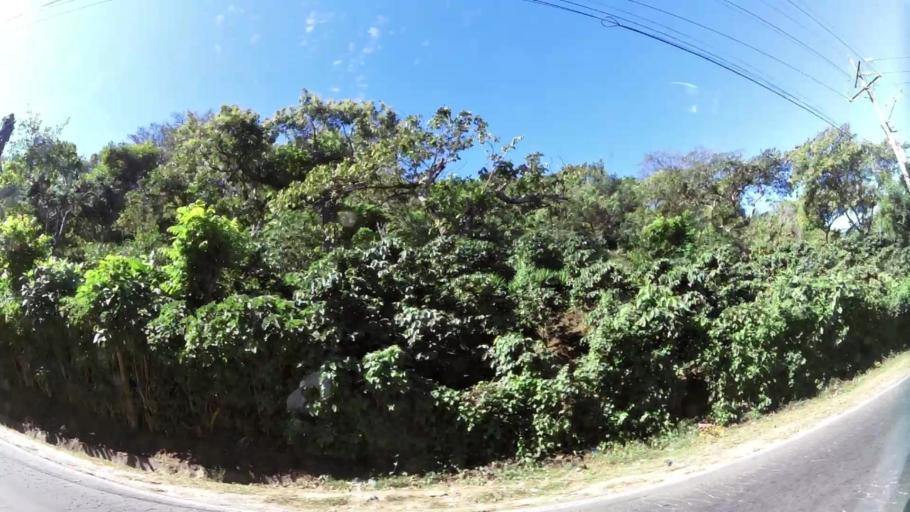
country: SV
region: Ahuachapan
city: Concepcion de Ataco
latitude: 13.8649
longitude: -89.8500
